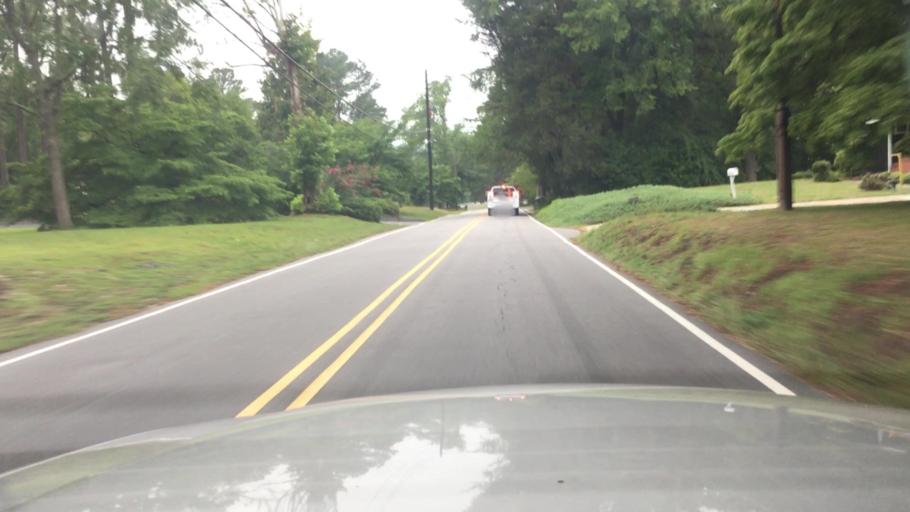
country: US
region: North Carolina
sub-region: Cumberland County
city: Hope Mills
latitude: 34.9736
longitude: -78.9421
